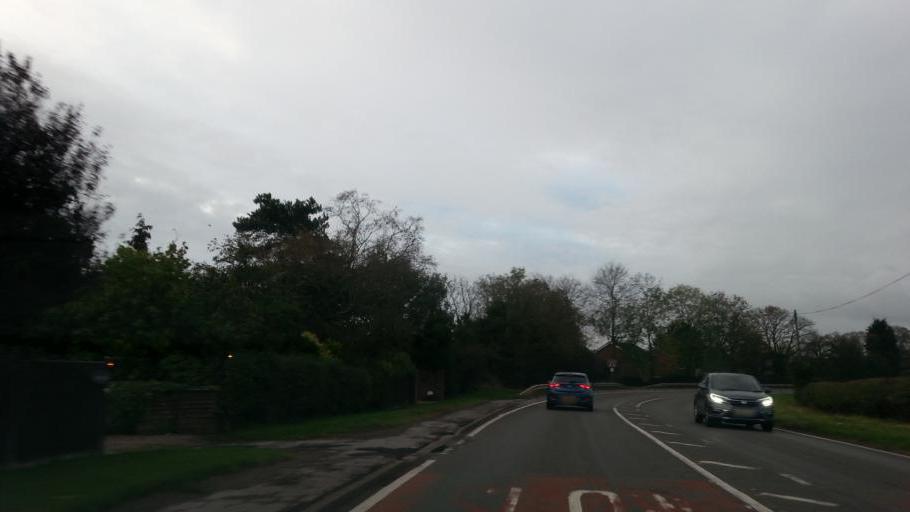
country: GB
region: England
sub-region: Nottinghamshire
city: Newark on Trent
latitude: 53.1090
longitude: -0.8199
